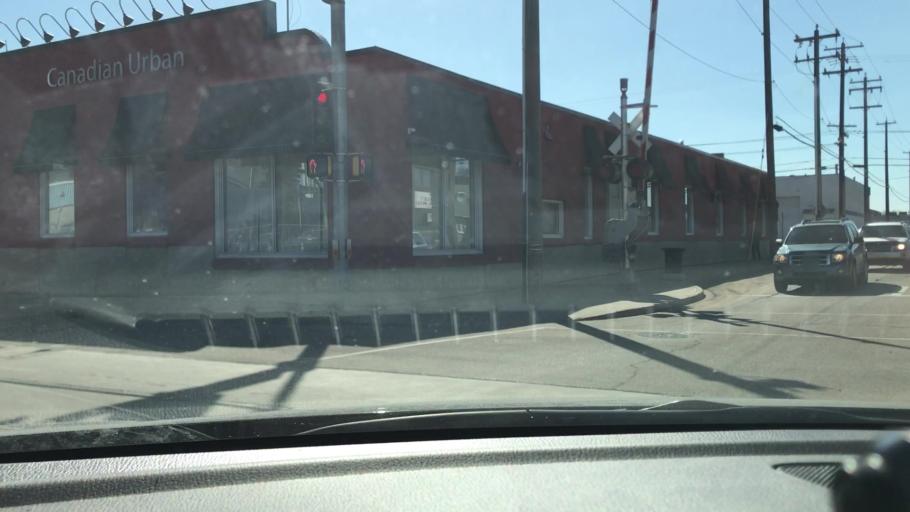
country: CA
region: Alberta
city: Edmonton
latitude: 53.5498
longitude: -113.5011
